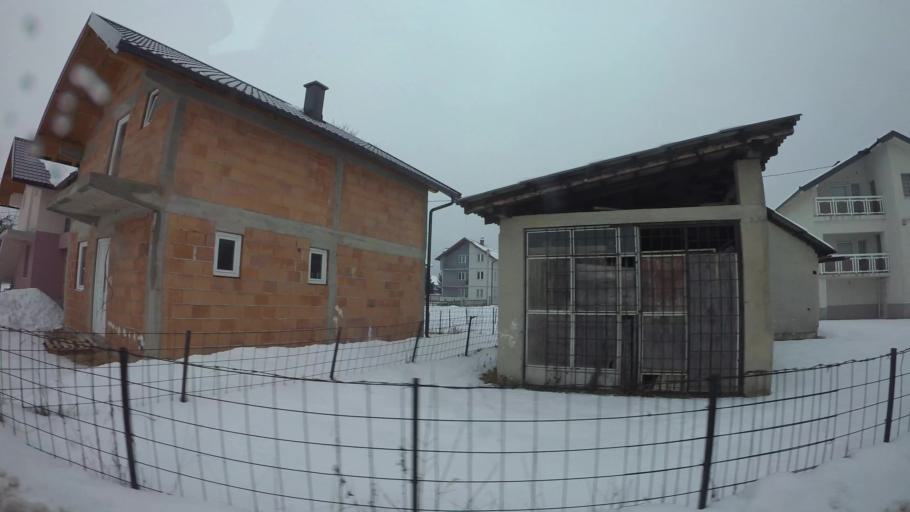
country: BA
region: Federation of Bosnia and Herzegovina
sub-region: Kanton Sarajevo
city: Sarajevo
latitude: 43.8361
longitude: 18.2848
